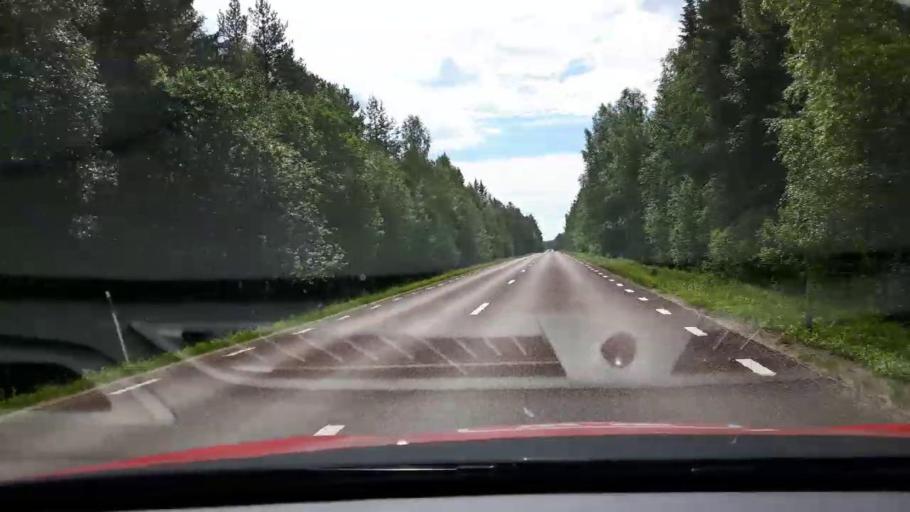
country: SE
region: Jaemtland
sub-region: Harjedalens Kommun
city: Sveg
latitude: 62.1159
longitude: 14.9701
